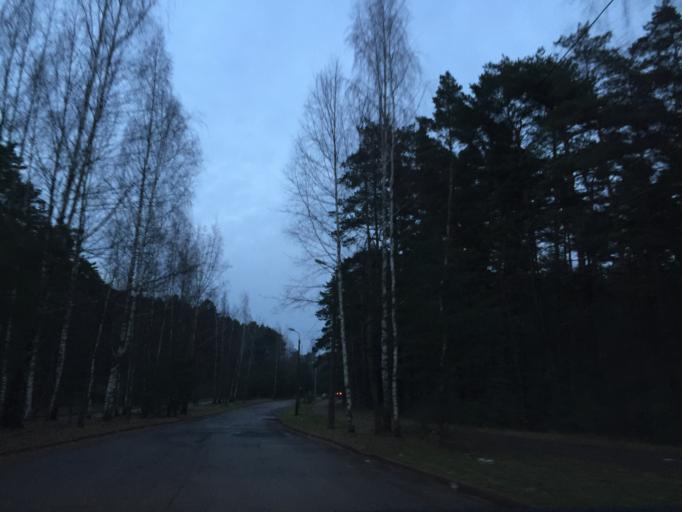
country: LV
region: Riga
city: Jaunciems
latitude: 57.0394
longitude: 24.1860
